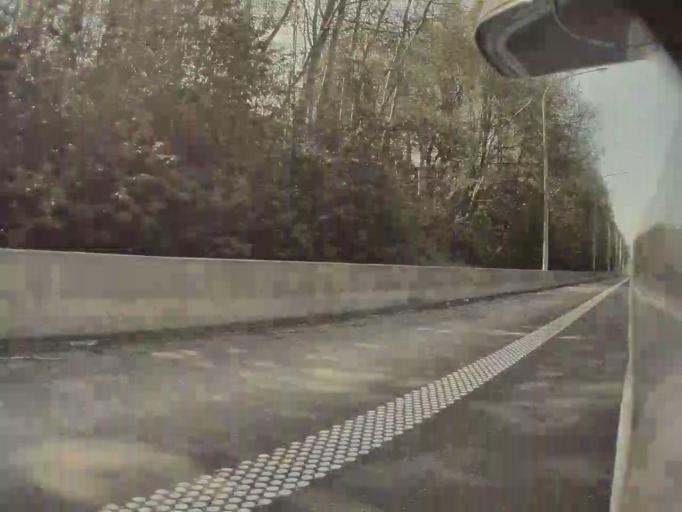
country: BE
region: Wallonia
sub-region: Province de Namur
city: Hamois
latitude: 50.2915
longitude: 5.1752
